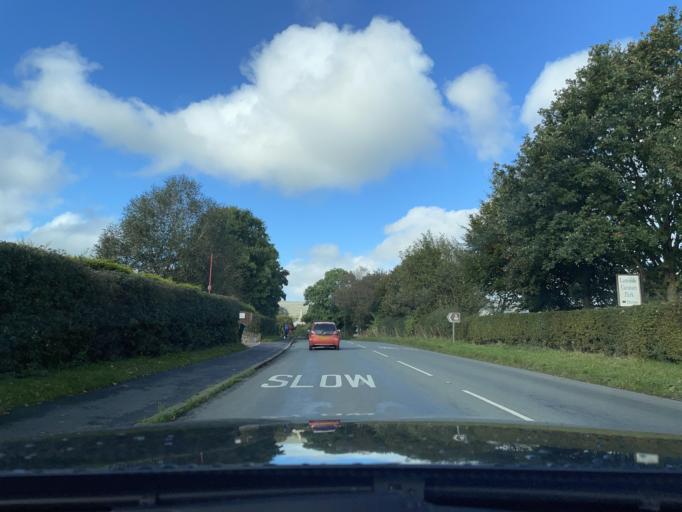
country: GB
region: England
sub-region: Derbyshire
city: Hope Valley
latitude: 53.3455
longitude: -1.7339
